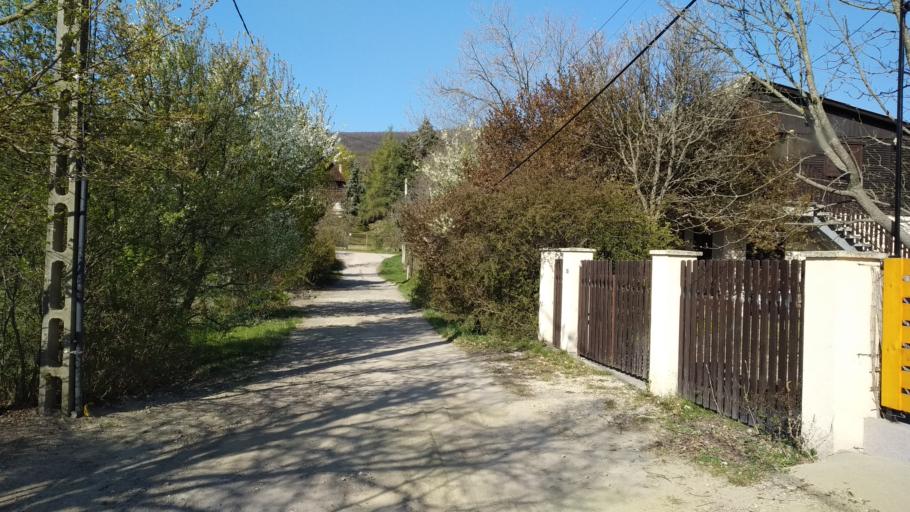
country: HU
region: Pest
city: Leanyfalu
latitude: 47.7096
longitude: 19.0819
